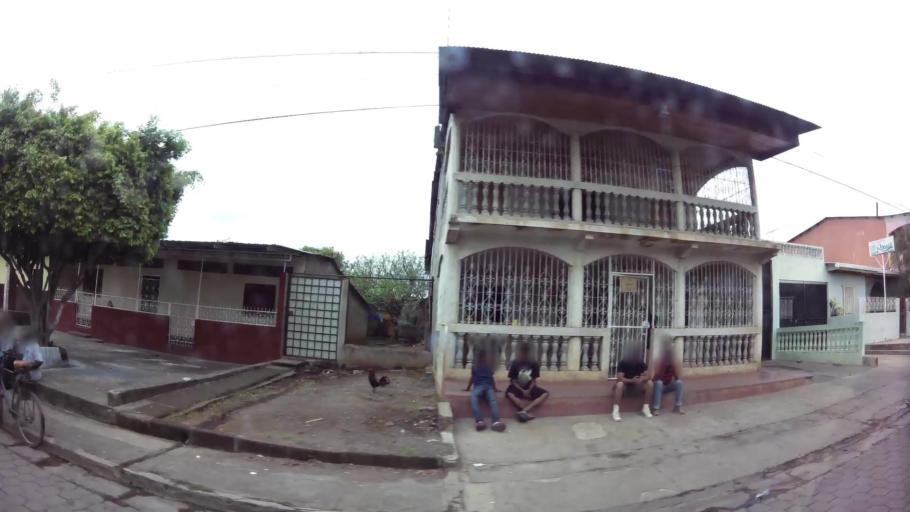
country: NI
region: Granada
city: Granada
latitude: 11.9415
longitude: -85.9524
